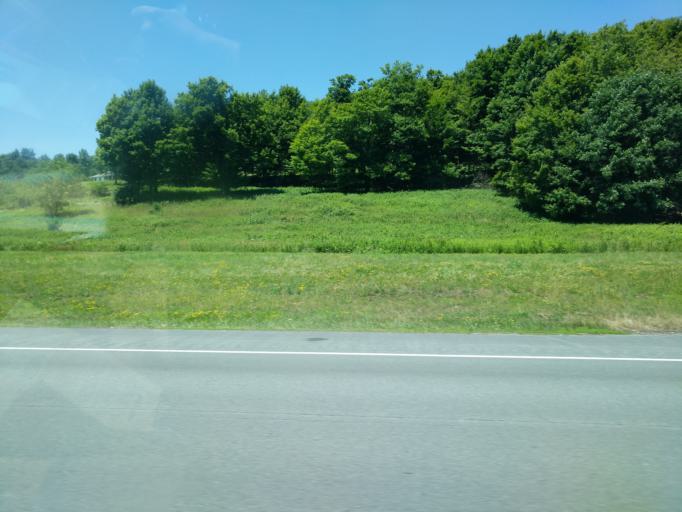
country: US
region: New York
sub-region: Sullivan County
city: Monticello
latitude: 41.6636
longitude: -74.6898
